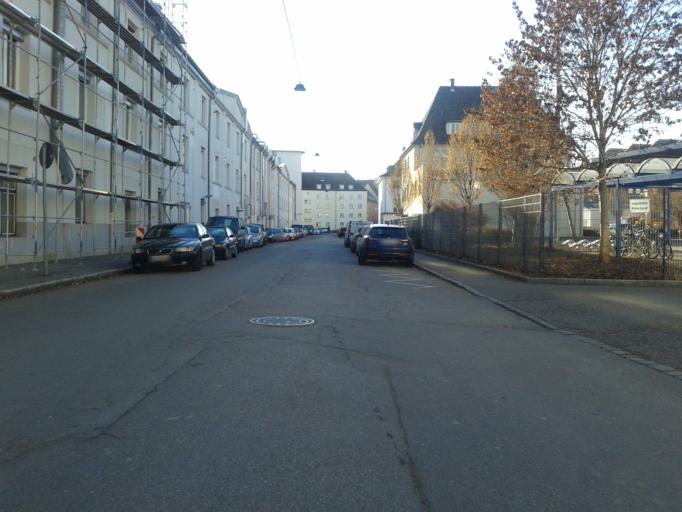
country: DE
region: Baden-Wuerttemberg
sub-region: Tuebingen Region
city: Ulm
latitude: 48.3969
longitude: 9.9709
